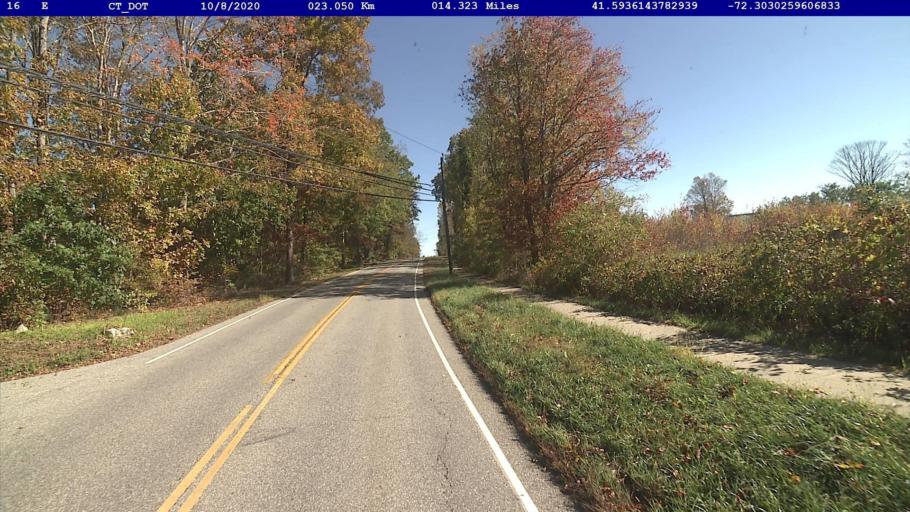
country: US
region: Connecticut
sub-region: New London County
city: Colchester
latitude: 41.5935
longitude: -72.3030
